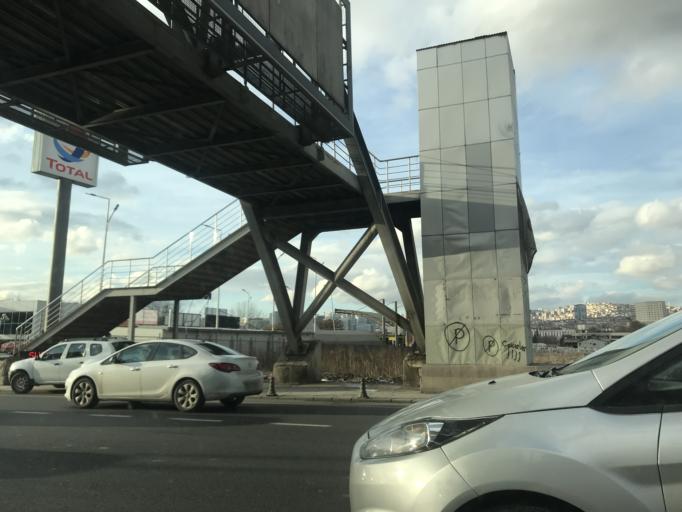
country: TR
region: Ankara
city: Ankara
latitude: 39.9567
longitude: 32.8464
